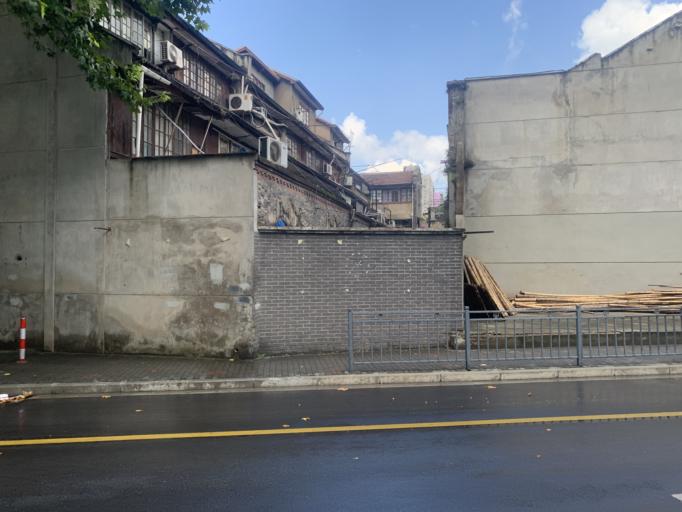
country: CN
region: Shanghai Shi
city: Luwan
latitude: 31.2128
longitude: 121.4737
